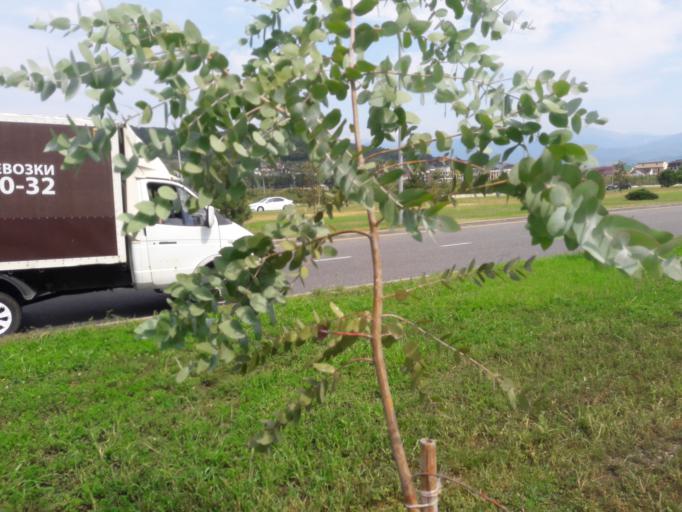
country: RU
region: Krasnodarskiy
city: Adler
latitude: 43.4050
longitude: 39.9762
